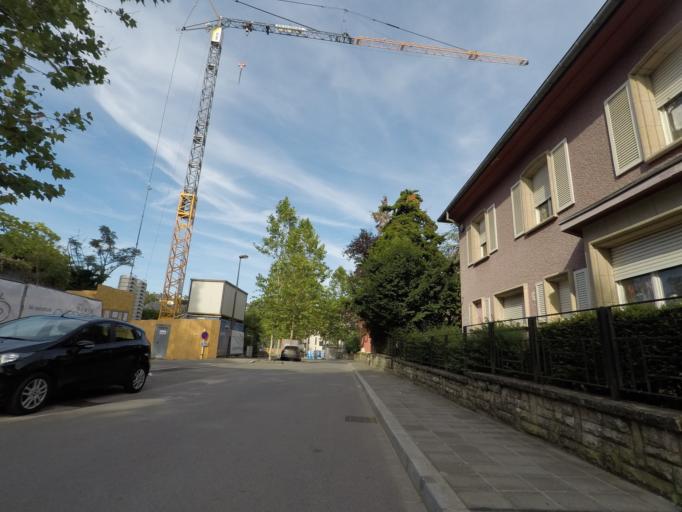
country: LU
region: Luxembourg
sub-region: Canton de Luxembourg
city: Luxembourg
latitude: 49.6010
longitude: 6.1227
